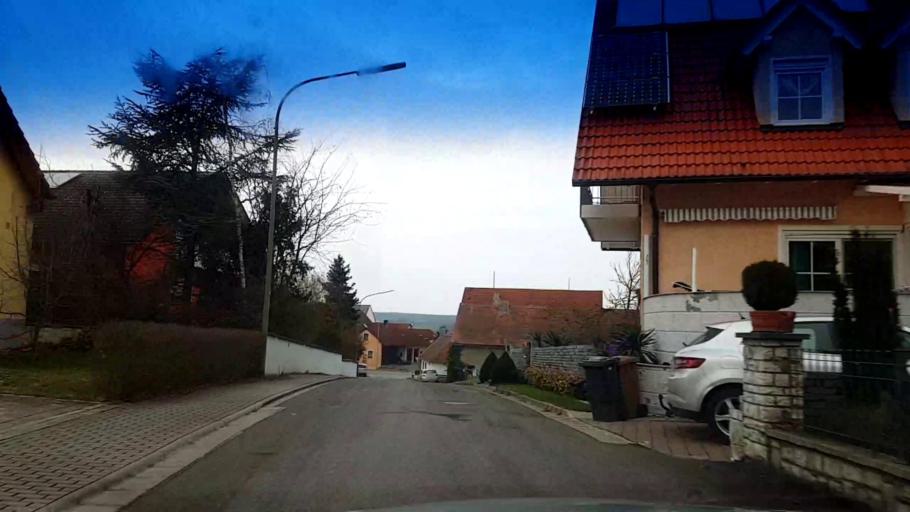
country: DE
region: Bavaria
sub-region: Upper Franconia
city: Pommersfelden
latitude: 49.8171
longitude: 10.8087
